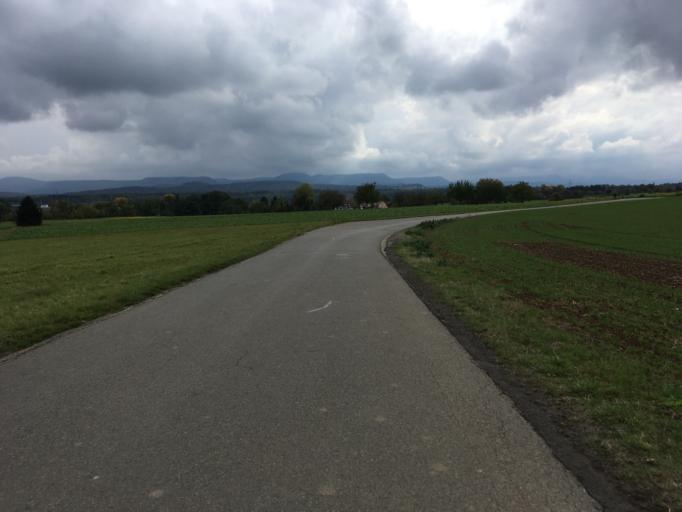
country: DE
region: Baden-Wuerttemberg
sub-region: Tuebingen Region
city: Kusterdingen
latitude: 48.5095
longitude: 9.1245
